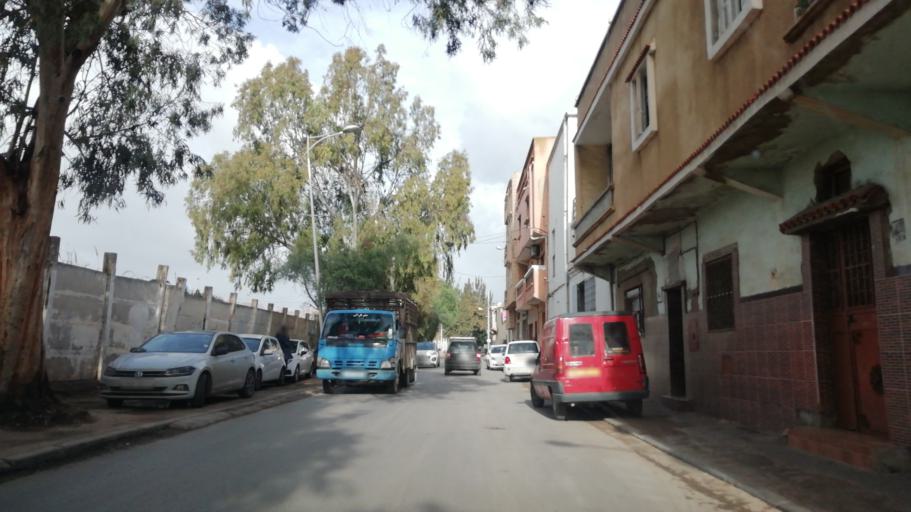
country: DZ
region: Oran
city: Oran
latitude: 35.6819
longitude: -0.6266
